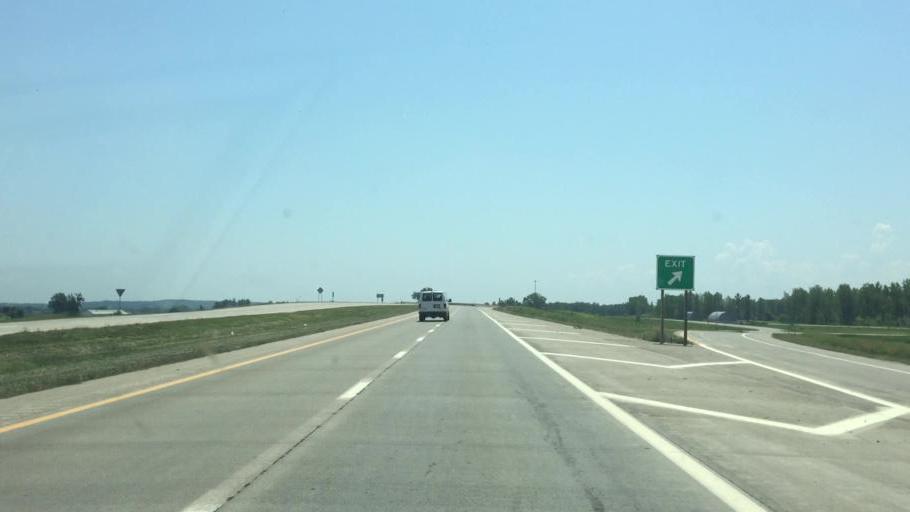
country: US
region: Kansas
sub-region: Doniphan County
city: Wathena
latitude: 39.7493
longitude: -94.9281
